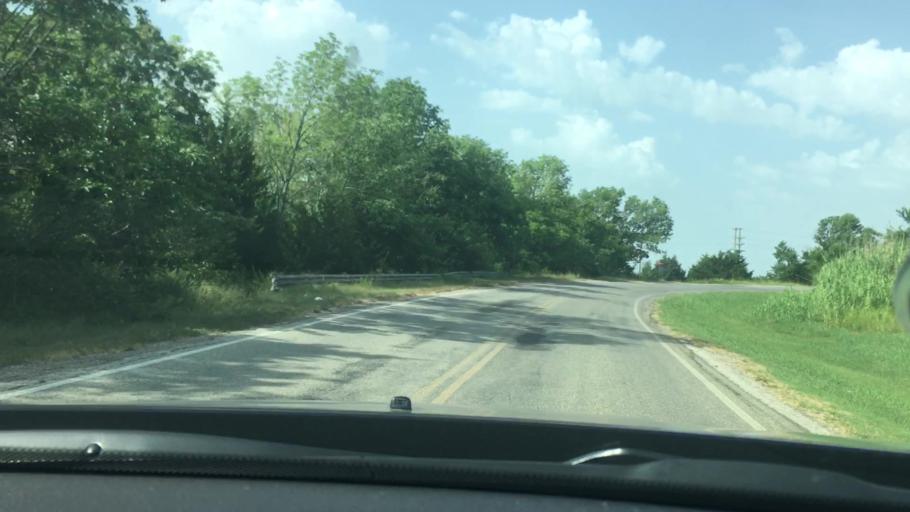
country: US
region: Oklahoma
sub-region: Pontotoc County
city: Byng
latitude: 34.8663
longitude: -96.5995
